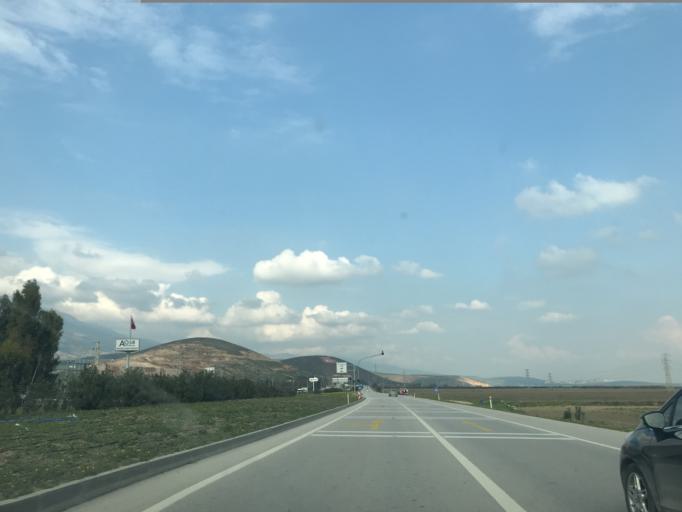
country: TR
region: Hatay
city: Serinyol
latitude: 36.4287
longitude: 36.2780
